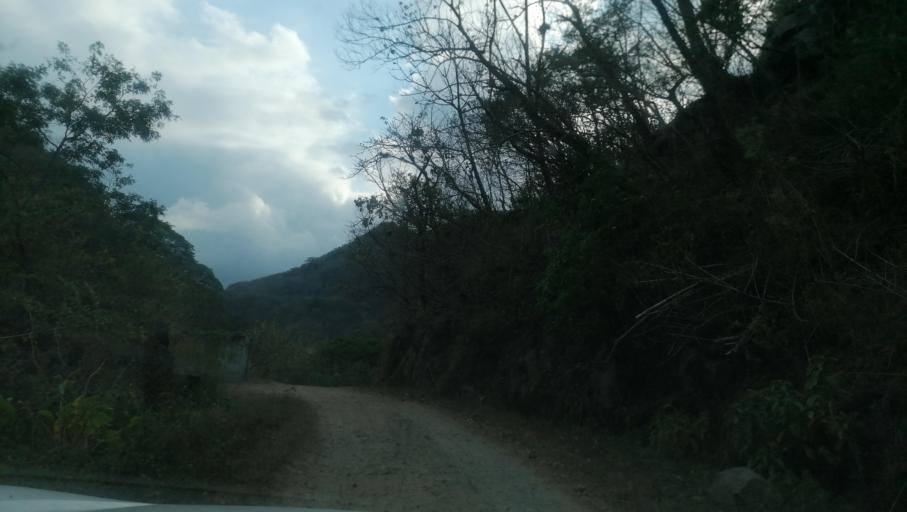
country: MX
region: Chiapas
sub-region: Cacahoatan
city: Benito Juarez
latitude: 15.1568
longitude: -92.1809
